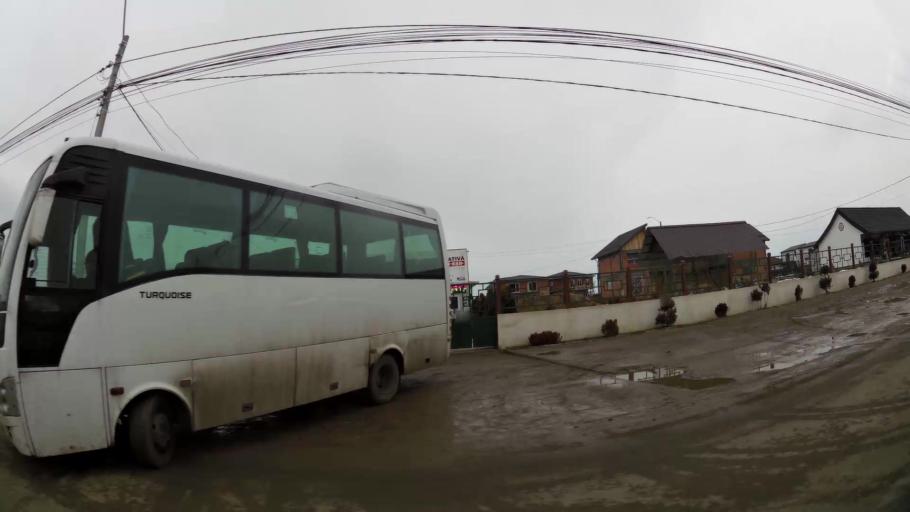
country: RO
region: Ilfov
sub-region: Comuna Tunari
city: Tunari
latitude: 44.5522
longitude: 26.1101
